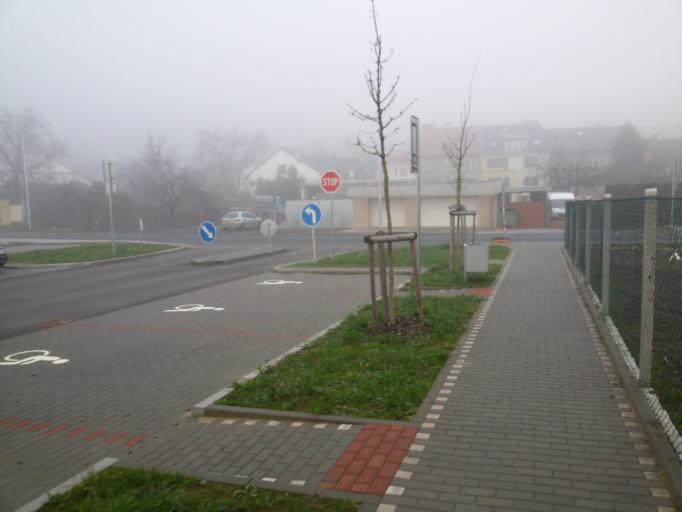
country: CZ
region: South Moravian
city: Tisnov
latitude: 49.3488
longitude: 16.4176
